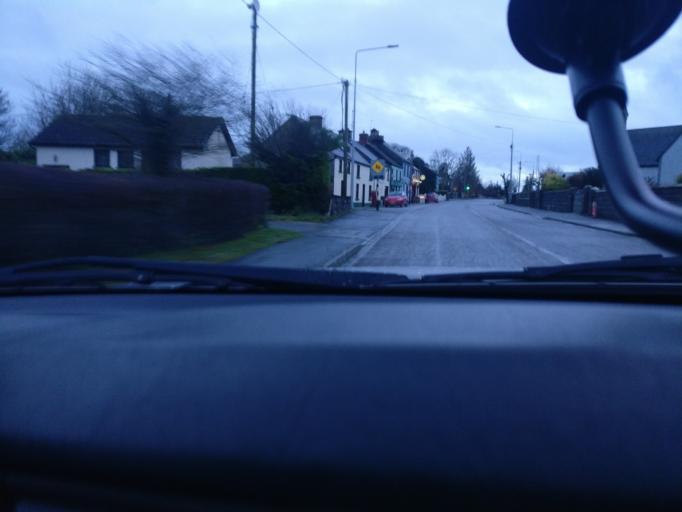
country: IE
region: Connaught
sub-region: County Galway
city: Loughrea
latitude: 53.2311
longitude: -8.4532
